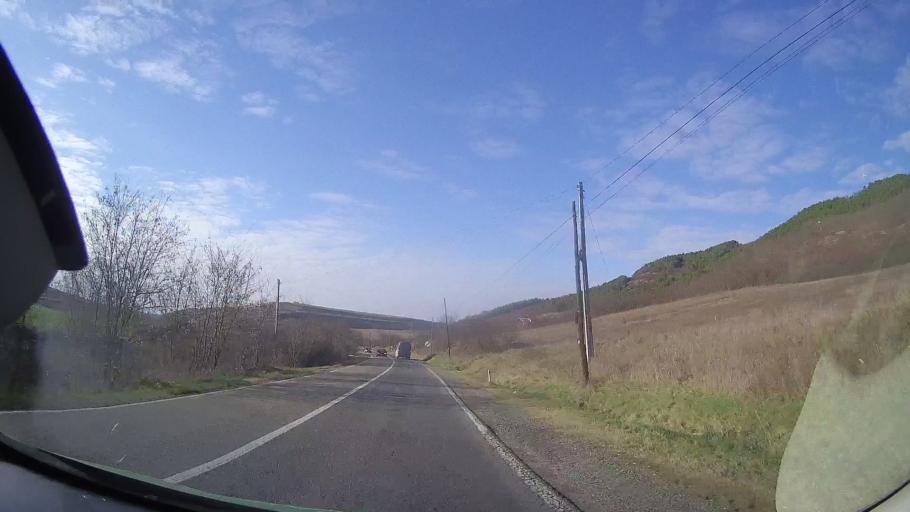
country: RO
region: Cluj
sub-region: Comuna Caianu
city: Caianu
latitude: 46.8011
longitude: 23.9382
